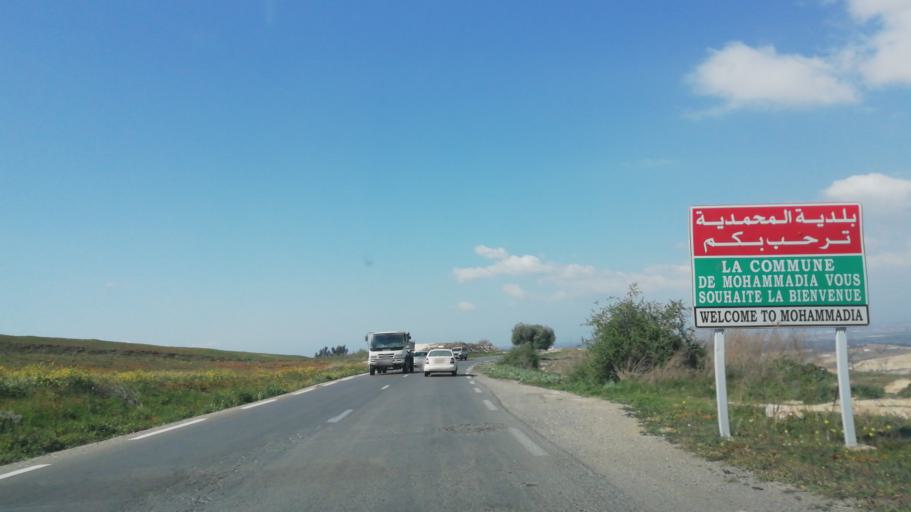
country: DZ
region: Mascara
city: Mascara
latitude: 35.5432
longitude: 0.0912
